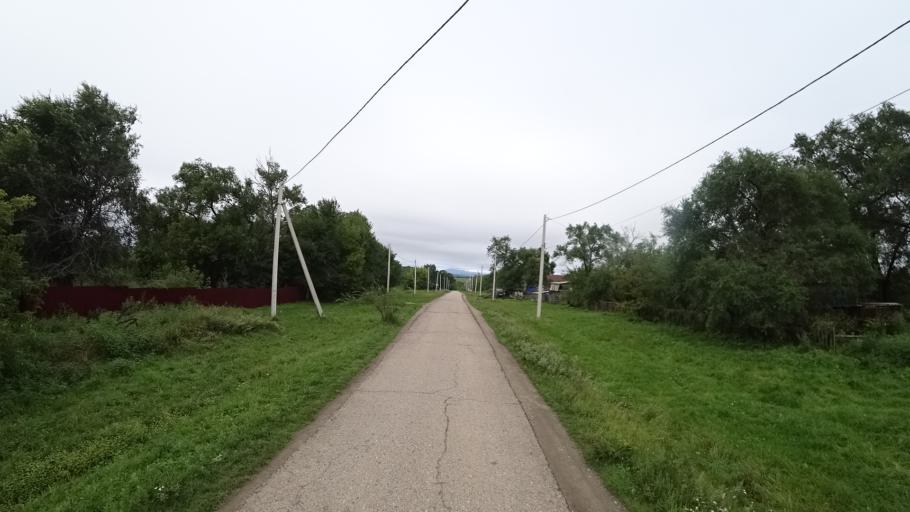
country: RU
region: Primorskiy
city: Monastyrishche
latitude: 44.0797
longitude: 132.5859
